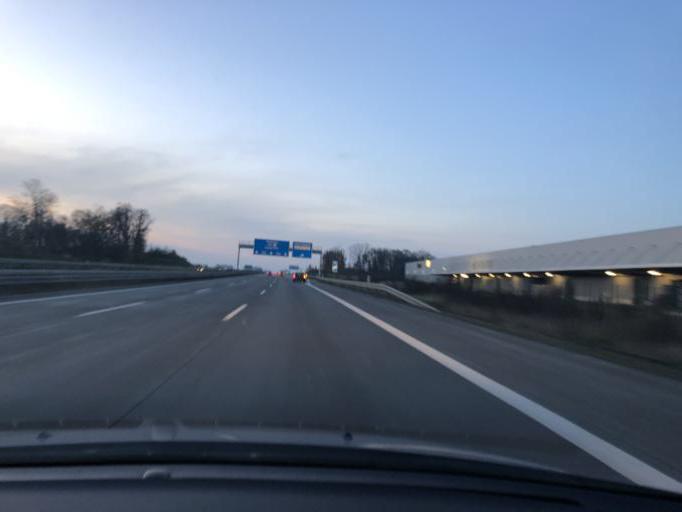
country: DE
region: Saxony
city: Taucha
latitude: 51.3945
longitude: 12.4325
